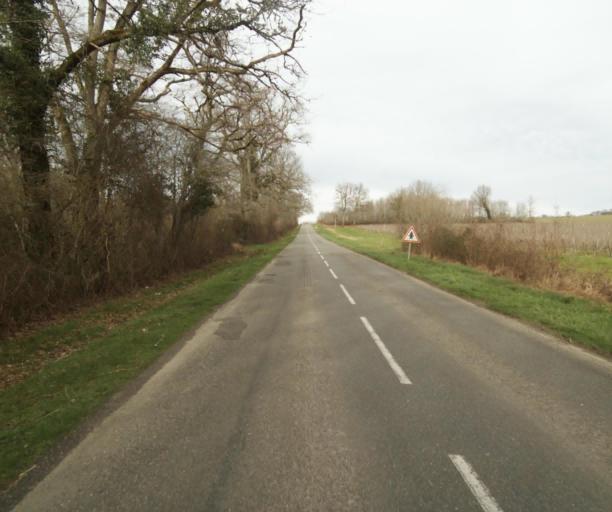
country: FR
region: Aquitaine
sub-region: Departement des Landes
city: Gabarret
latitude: 43.9567
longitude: 0.0078
